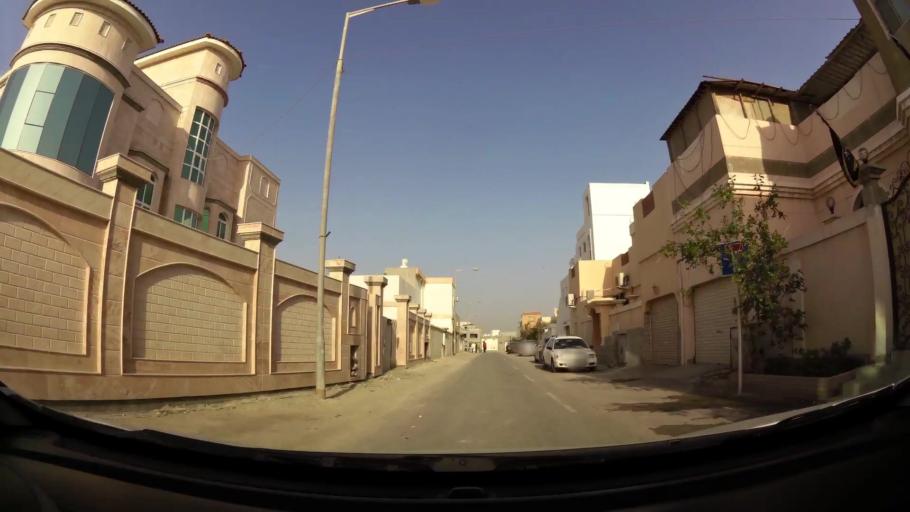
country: BH
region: Manama
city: Jidd Hafs
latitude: 26.2164
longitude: 50.4983
